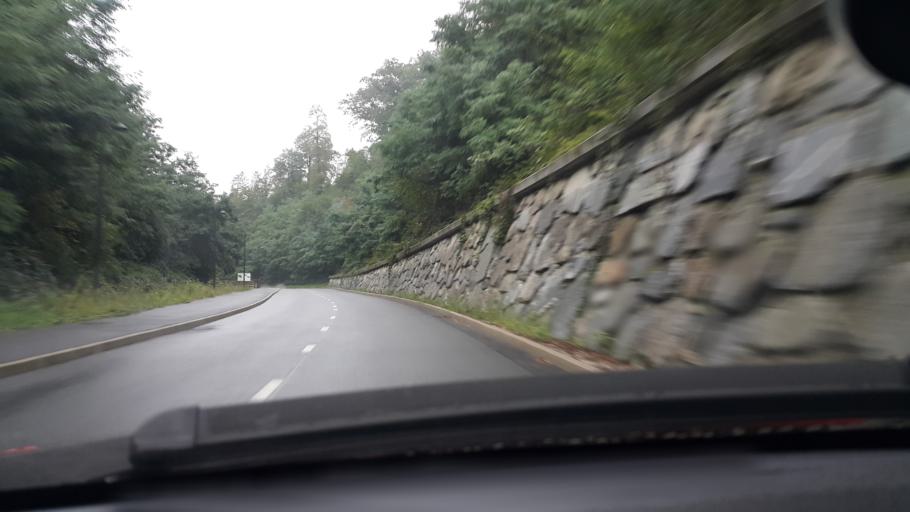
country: SI
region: Maribor
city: Maribor
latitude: 46.5678
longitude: 15.6447
